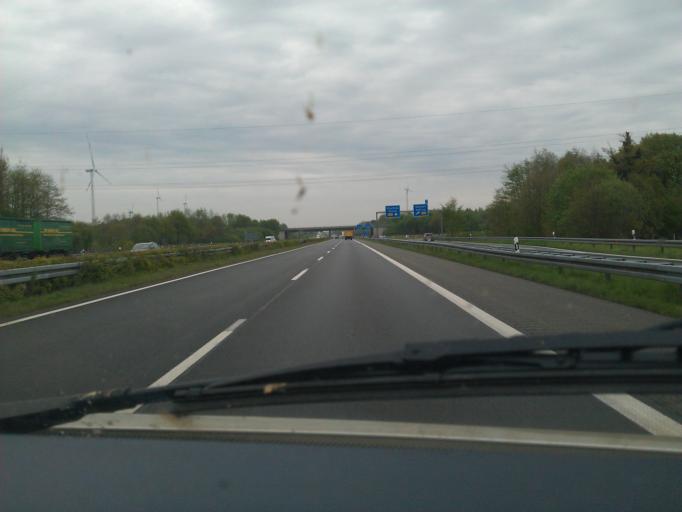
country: DE
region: North Rhine-Westphalia
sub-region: Regierungsbezirk Munster
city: Heek
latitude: 52.1881
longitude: 7.1136
